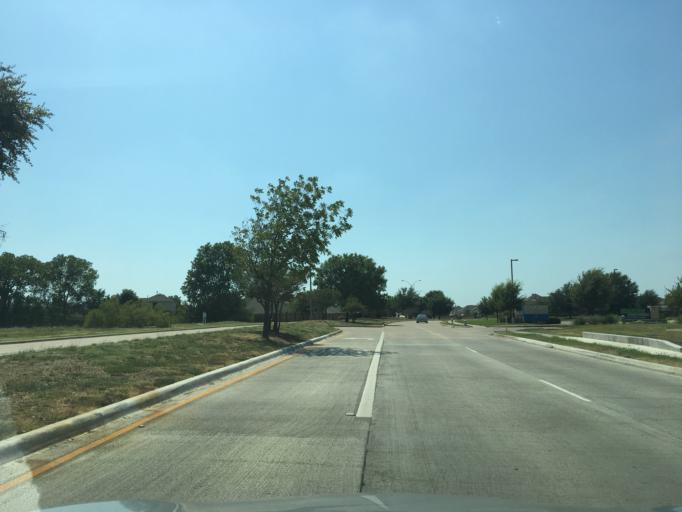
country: US
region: Texas
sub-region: Tarrant County
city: Everman
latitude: 32.5993
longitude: -97.3213
